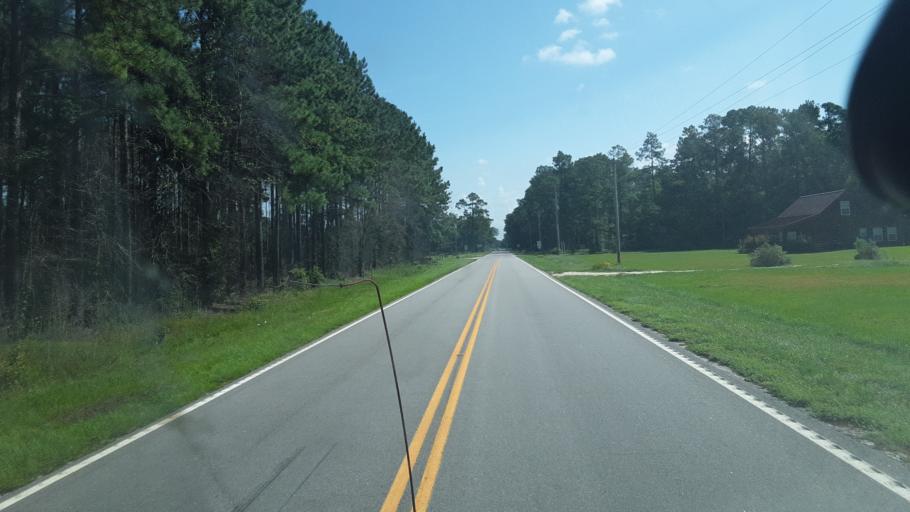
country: US
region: South Carolina
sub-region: Hampton County
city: Varnville
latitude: 32.8765
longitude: -81.0415
